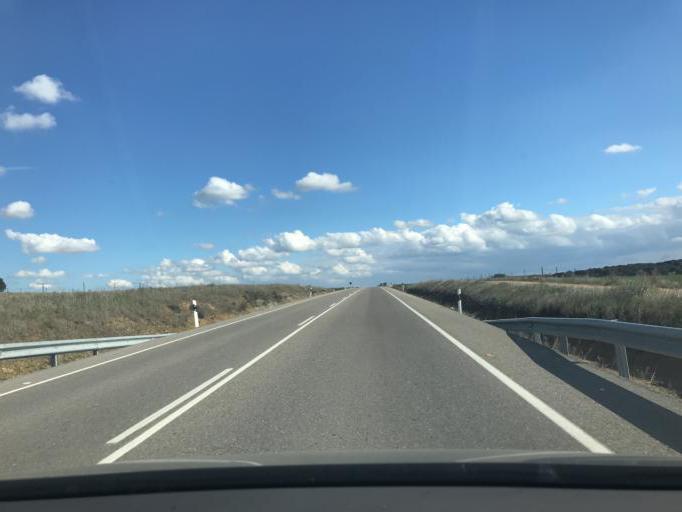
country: ES
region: Extremadura
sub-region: Provincia de Badajoz
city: Granja de Torrehermosa
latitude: 38.2912
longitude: -5.5347
